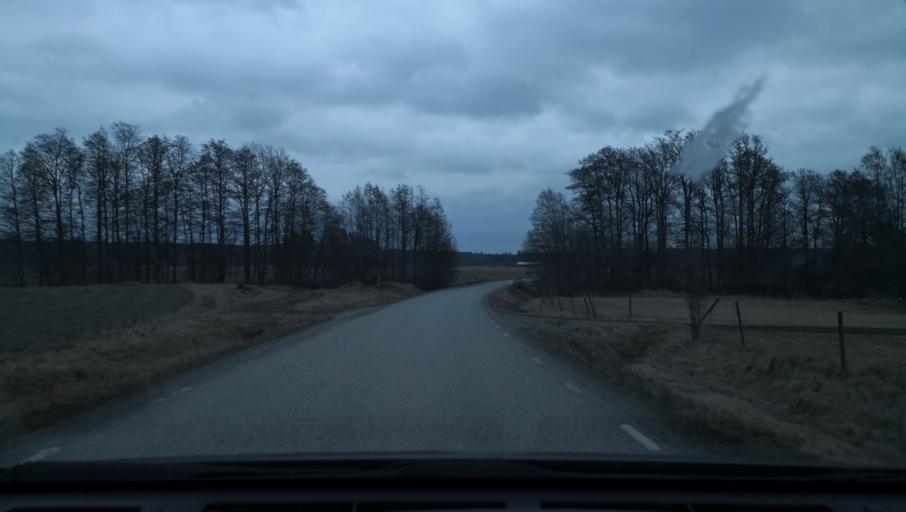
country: SE
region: OErebro
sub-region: Lindesbergs Kommun
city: Fellingsbro
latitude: 59.5616
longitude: 15.5824
